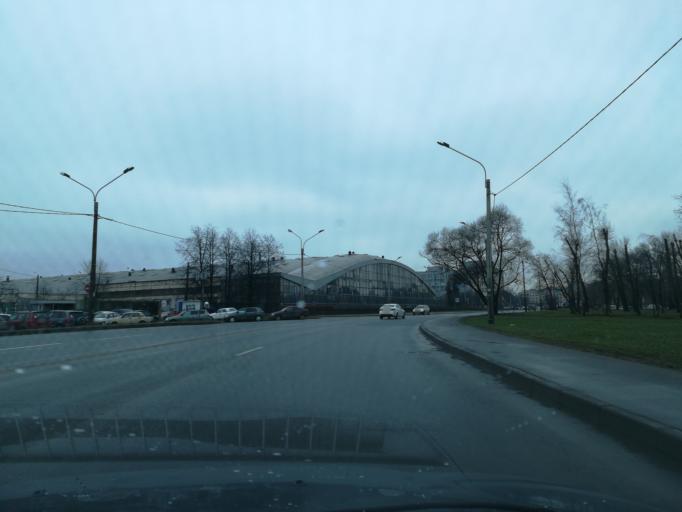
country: RU
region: St.-Petersburg
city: Avtovo
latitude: 59.8615
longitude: 30.2613
